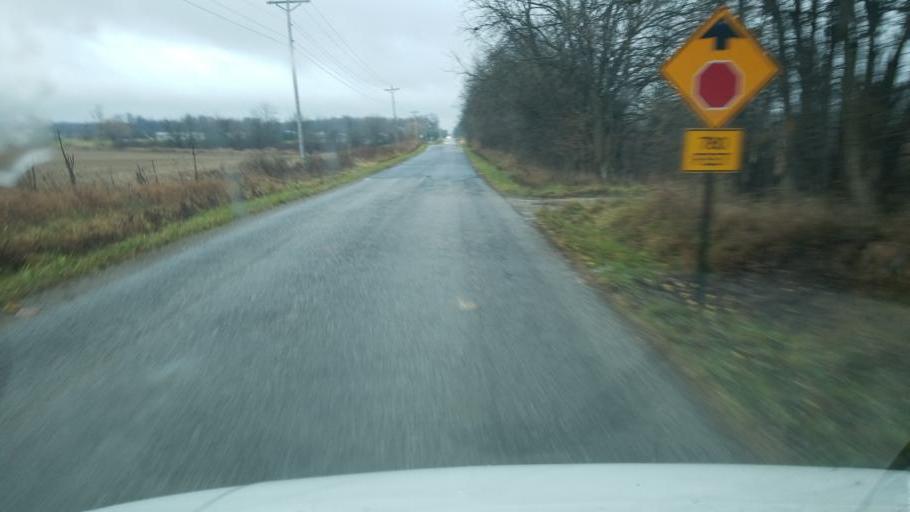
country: US
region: Ohio
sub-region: Morrow County
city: Mount Gilead
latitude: 40.4636
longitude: -82.7831
